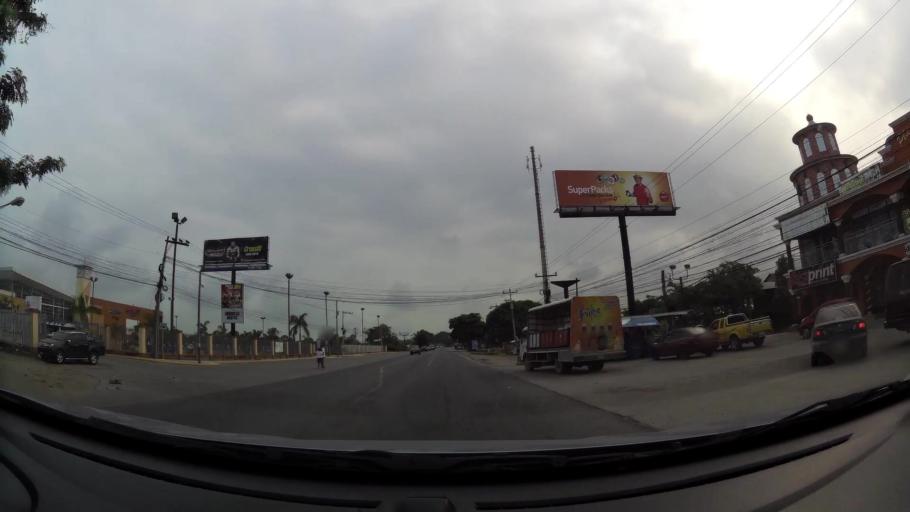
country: HN
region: Yoro
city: El Progreso
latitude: 15.4193
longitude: -87.8007
